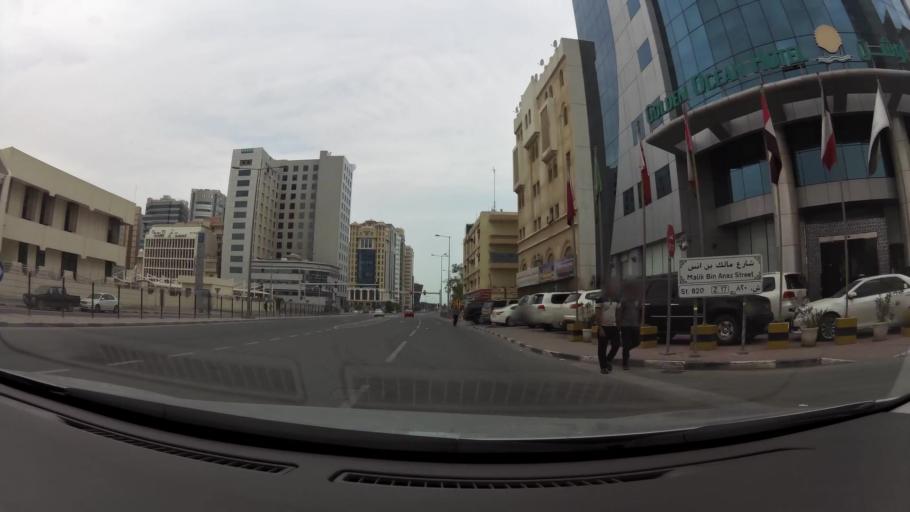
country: QA
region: Baladiyat ad Dawhah
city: Doha
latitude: 25.2858
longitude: 51.5442
